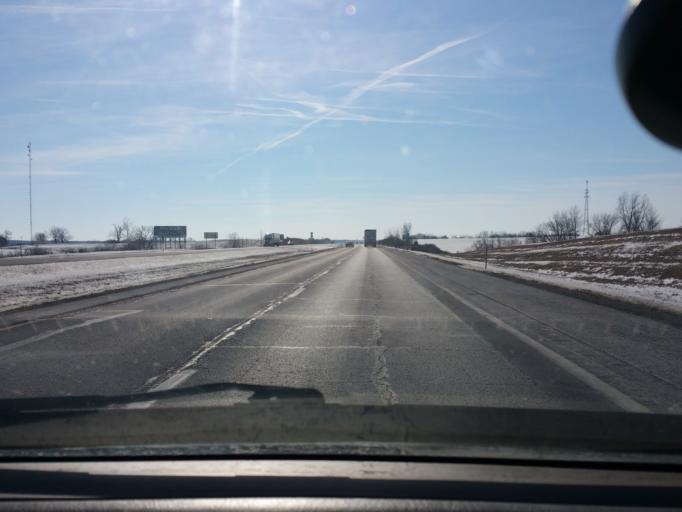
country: US
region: Missouri
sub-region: Harrison County
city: Bethany
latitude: 40.2606
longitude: -94.0130
